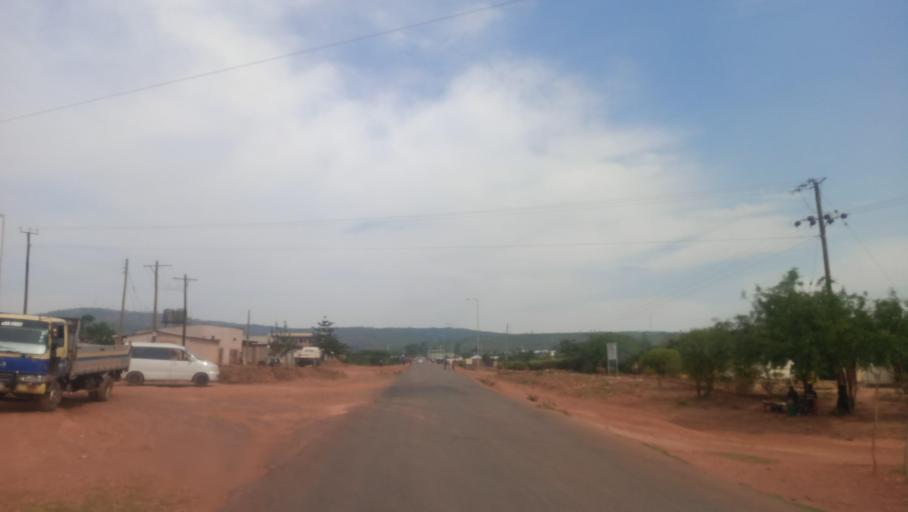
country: ZM
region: Northern
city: Mpika
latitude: -11.8415
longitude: 31.4392
